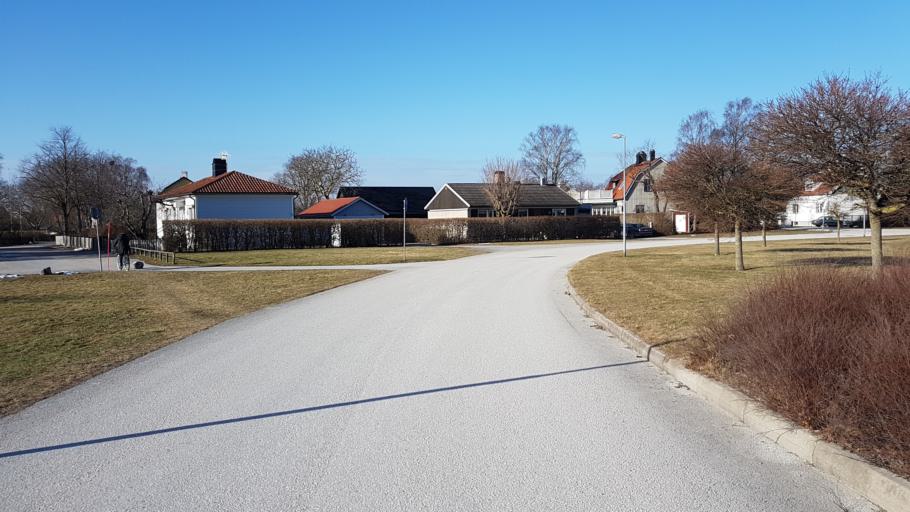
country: SE
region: Gotland
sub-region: Gotland
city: Visby
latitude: 57.6313
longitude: 18.3199
